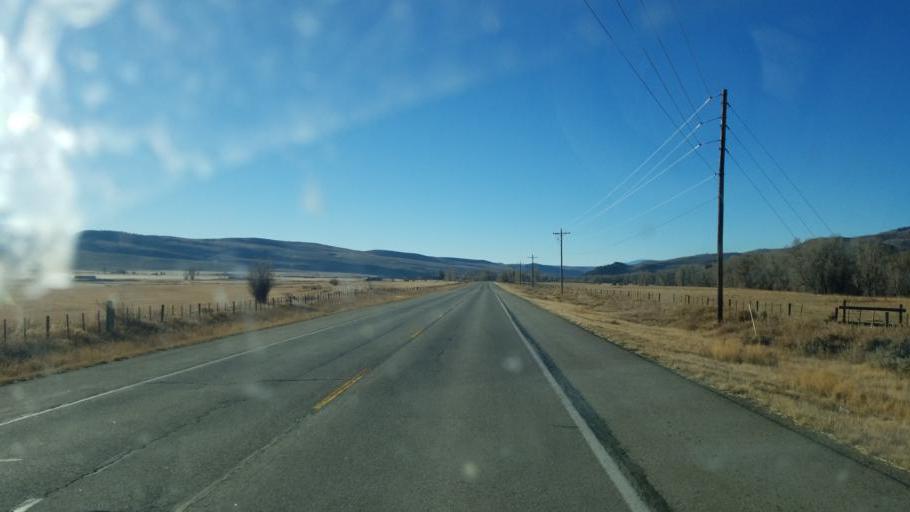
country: US
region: Colorado
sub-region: Gunnison County
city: Crested Butte
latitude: 38.7574
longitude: -106.8619
